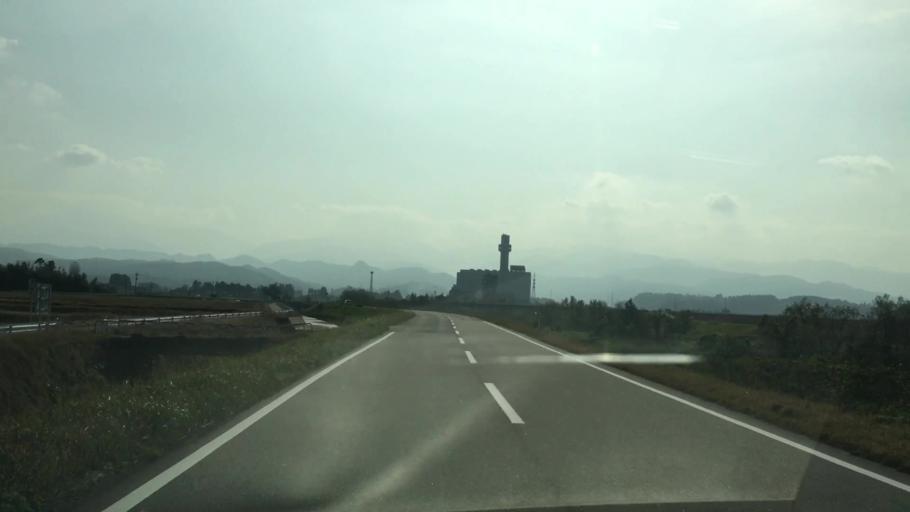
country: JP
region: Toyama
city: Kamiichi
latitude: 36.6306
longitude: 137.2973
